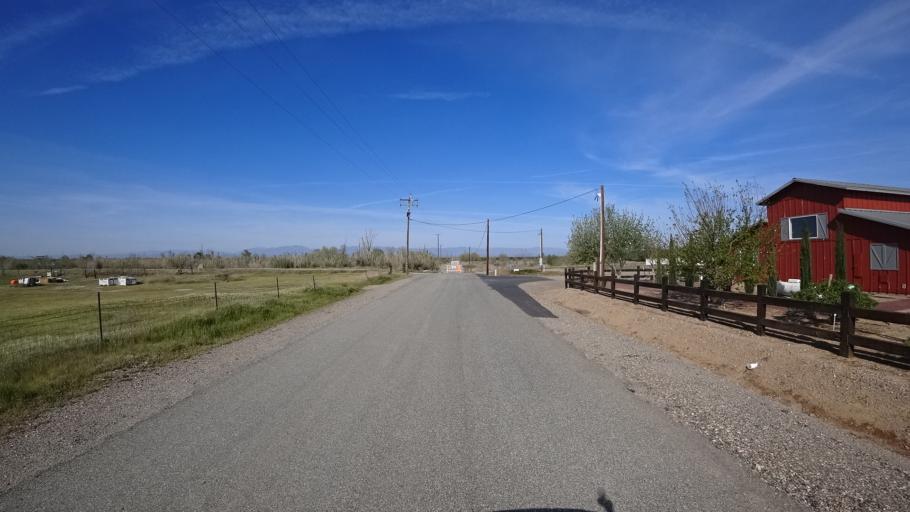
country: US
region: California
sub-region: Glenn County
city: Willows
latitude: 39.6113
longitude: -122.1975
